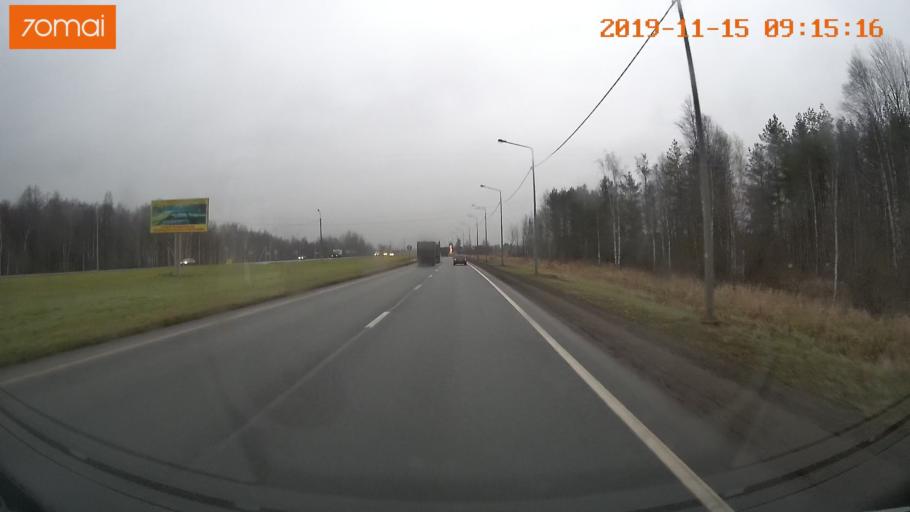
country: RU
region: Vologda
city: Tonshalovo
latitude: 59.2369
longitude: 37.9658
